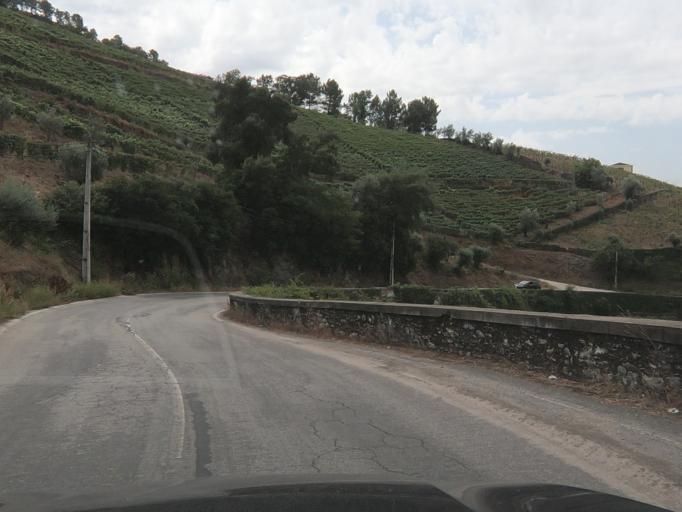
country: PT
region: Vila Real
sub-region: Santa Marta de Penaguiao
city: Santa Marta de Penaguiao
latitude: 41.2318
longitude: -7.7647
